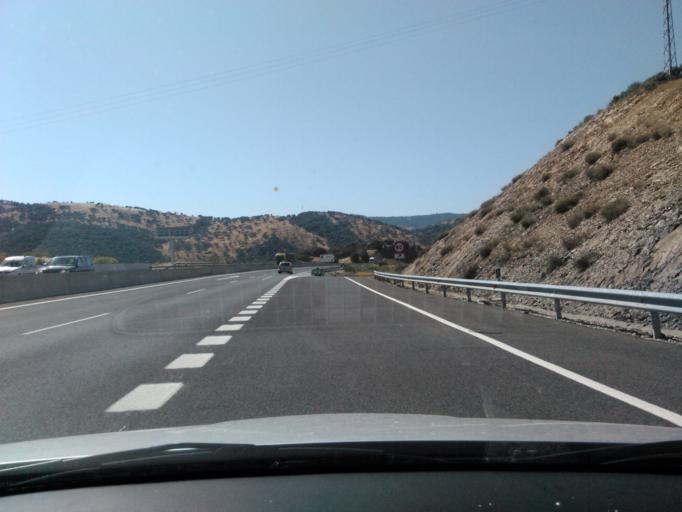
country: ES
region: Andalusia
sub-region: Provincia de Jaen
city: Santa Elena
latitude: 38.4166
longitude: -3.4996
